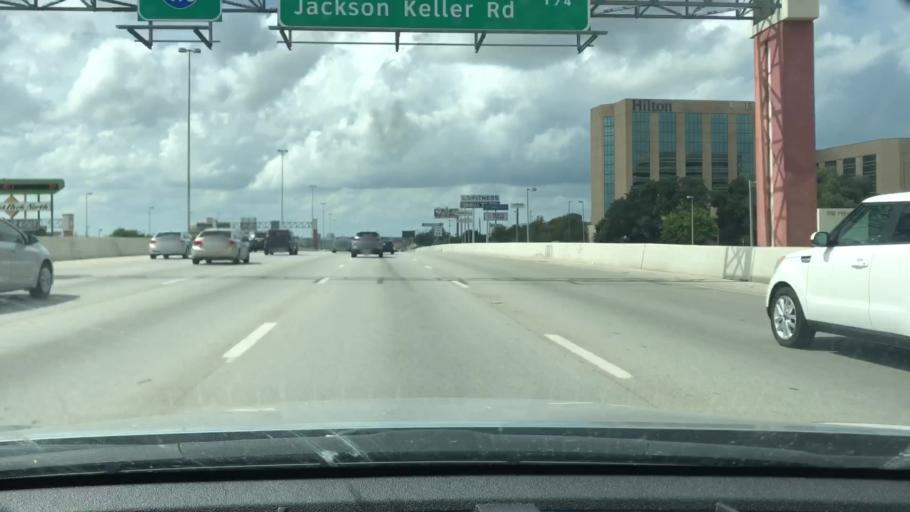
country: US
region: Texas
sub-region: Bexar County
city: Castle Hills
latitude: 29.5210
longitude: -98.5015
